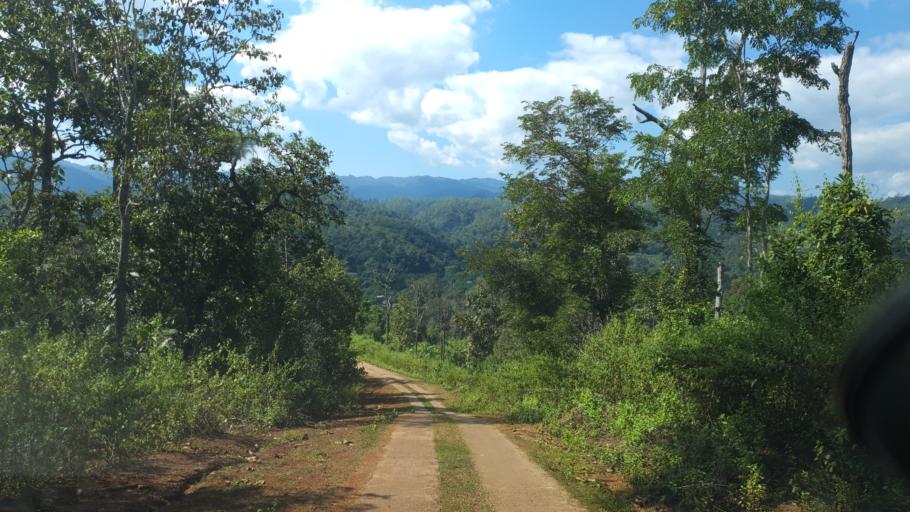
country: TH
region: Chiang Mai
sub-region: Amphoe Chiang Dao
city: Chiang Dao
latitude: 19.2965
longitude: 98.7129
